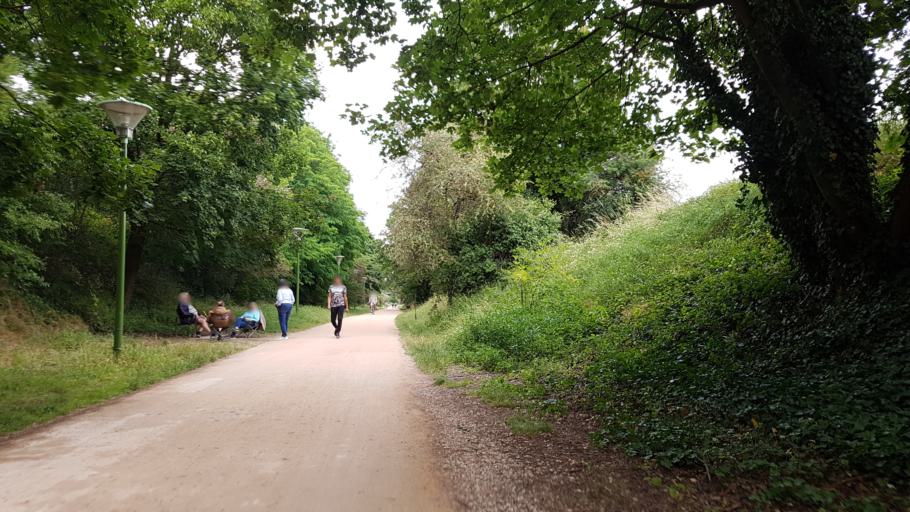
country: FR
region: Rhone-Alpes
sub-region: Departement du Rhone
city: Sathonay-Camp
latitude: 45.8076
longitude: 4.8587
